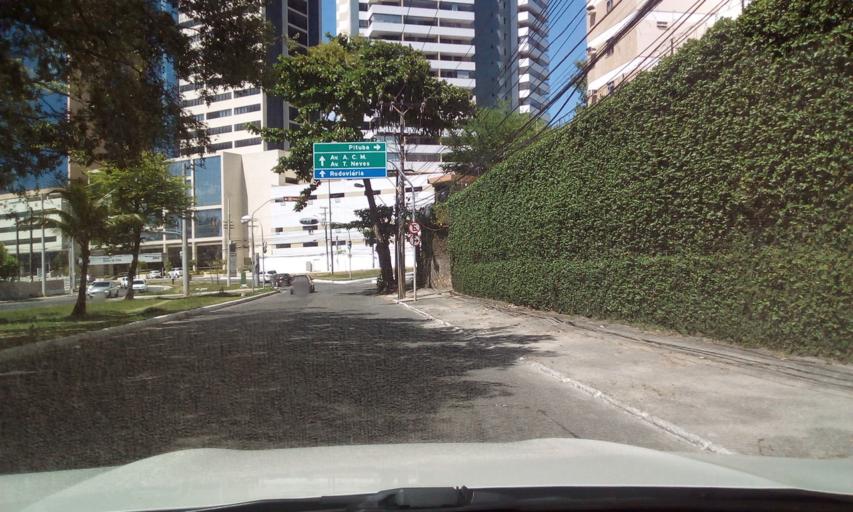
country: BR
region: Bahia
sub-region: Salvador
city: Salvador
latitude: -12.9899
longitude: -38.4666
